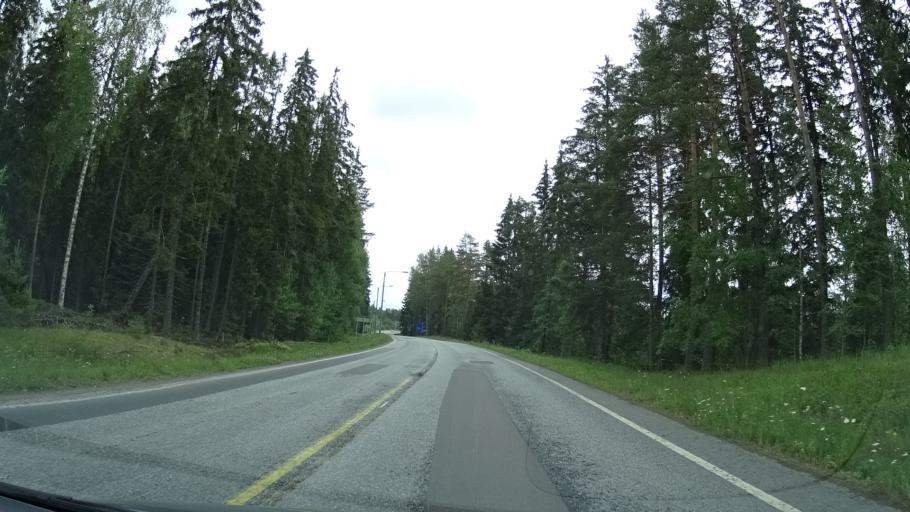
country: FI
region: Pirkanmaa
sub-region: Etelae-Pirkanmaa
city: Urjala
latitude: 61.0832
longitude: 23.5259
